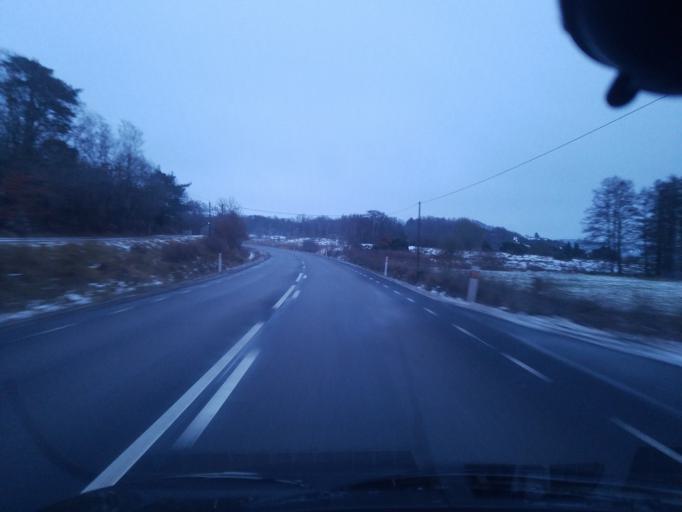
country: SE
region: Vaestra Goetaland
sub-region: Lysekils Kommun
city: Lysekil
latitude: 58.3047
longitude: 11.4912
